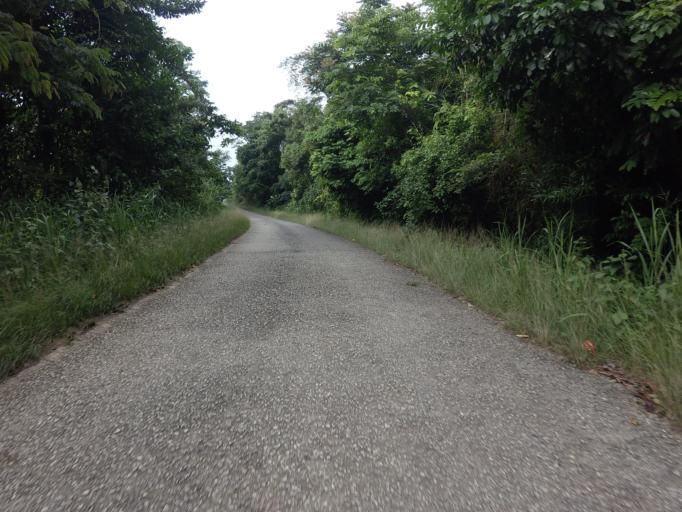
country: GH
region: Volta
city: Kpandu
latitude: 6.8363
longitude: 0.4269
